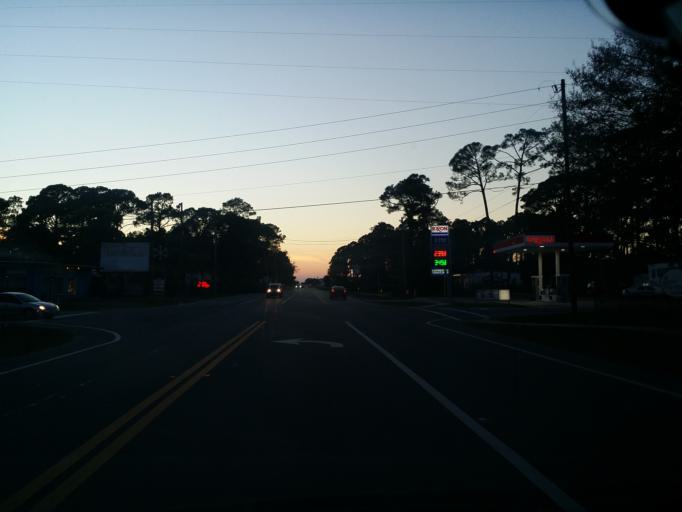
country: US
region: Florida
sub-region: Franklin County
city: Eastpoint
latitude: 29.7362
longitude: -84.8876
